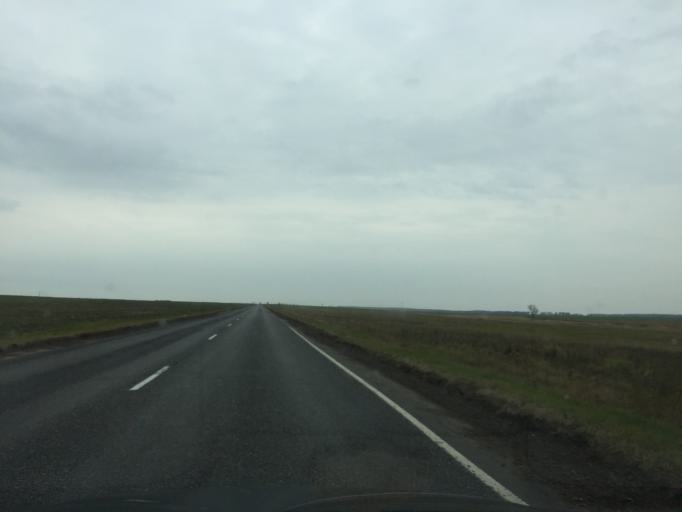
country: BY
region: Gomel
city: Dowsk
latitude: 53.1852
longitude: 30.5012
